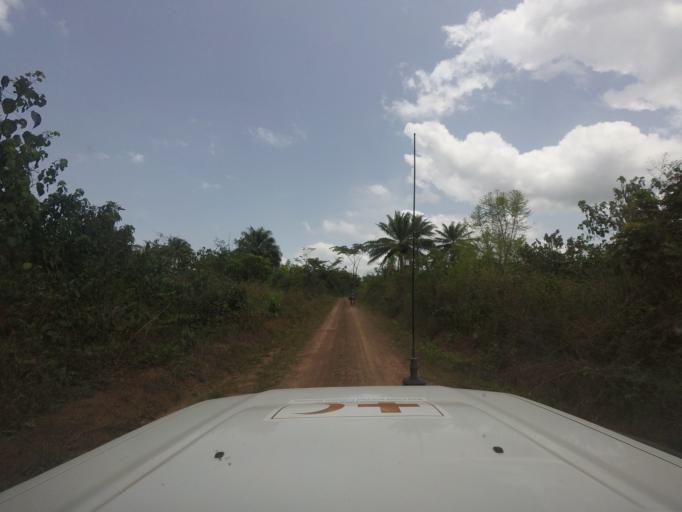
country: GN
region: Nzerekore
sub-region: Yomou
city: Yomou
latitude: 7.2736
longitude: -9.1857
